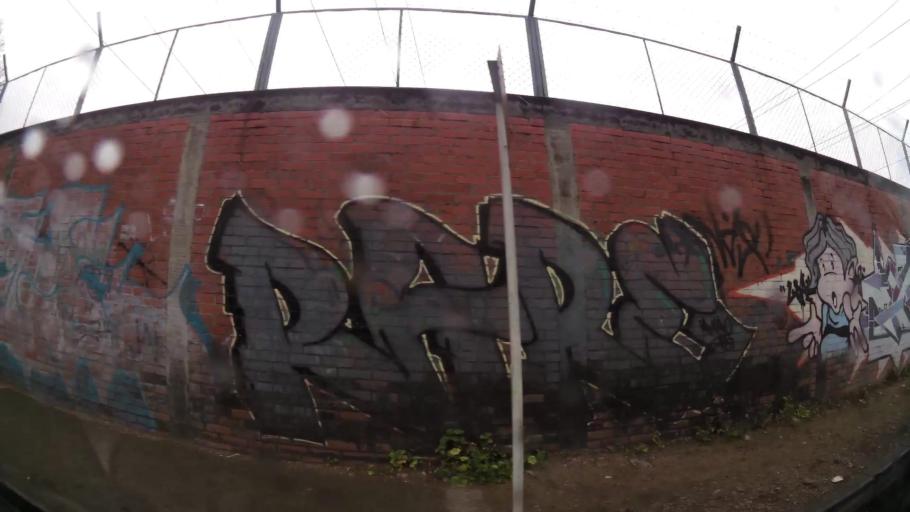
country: CO
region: Bogota D.C.
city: Bogota
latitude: 4.6589
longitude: -74.1002
